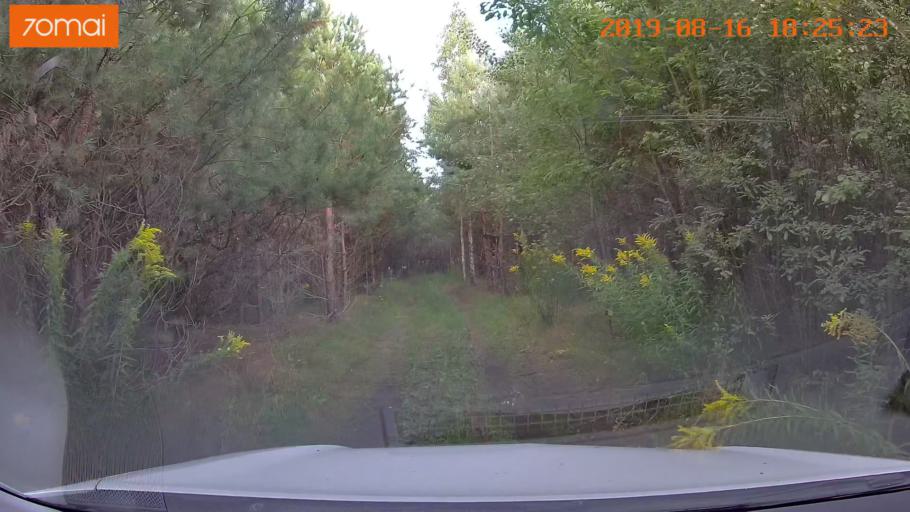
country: BY
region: Mogilev
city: Asipovichy
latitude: 53.2038
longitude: 28.6376
